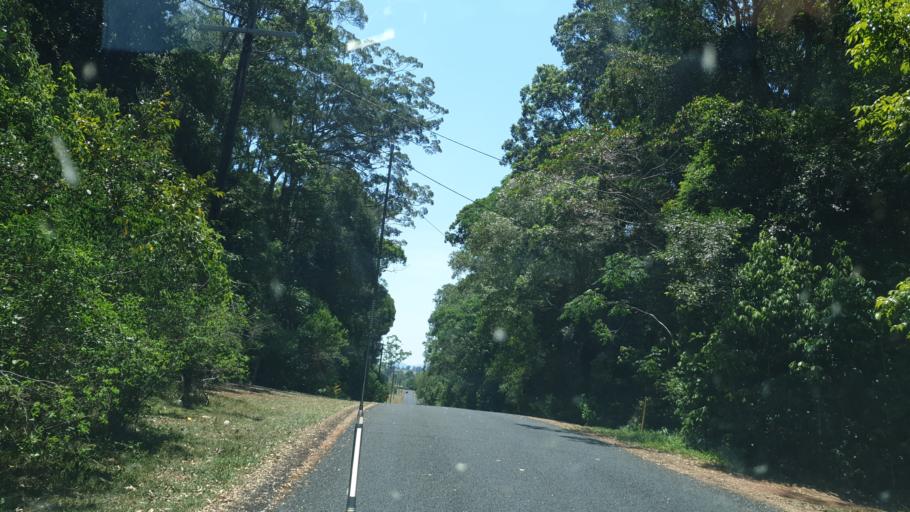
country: AU
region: Queensland
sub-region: Tablelands
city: Atherton
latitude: -17.3415
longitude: 145.6264
